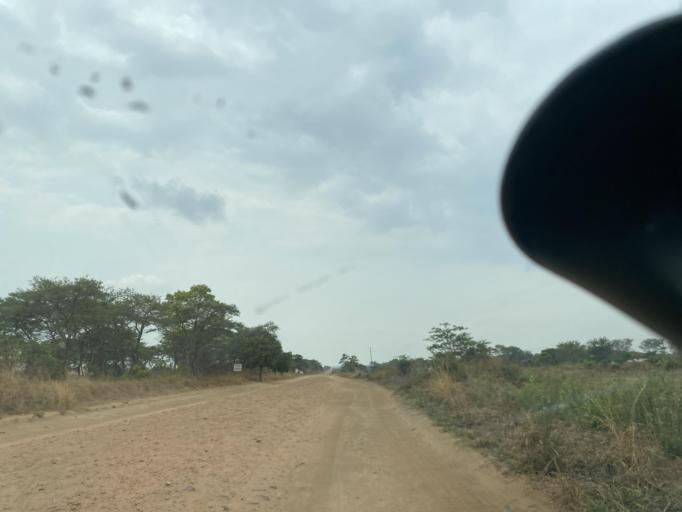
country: ZM
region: Lusaka
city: Lusaka
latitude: -15.2306
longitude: 28.3354
